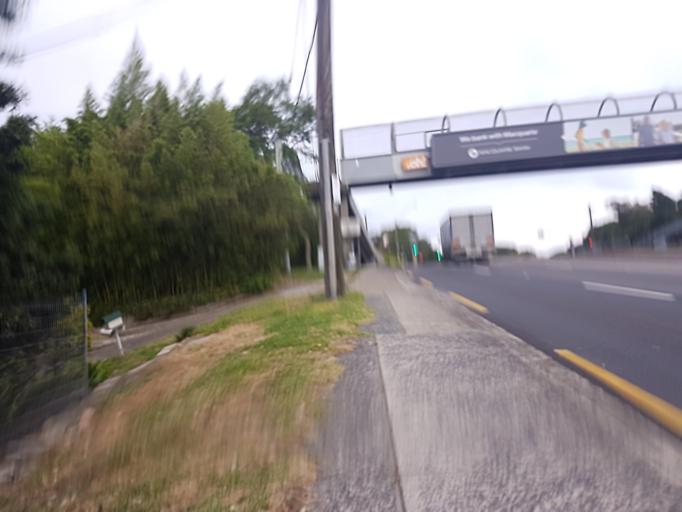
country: AU
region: New South Wales
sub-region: Warringah
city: Forestville
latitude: -33.7608
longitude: 151.2083
